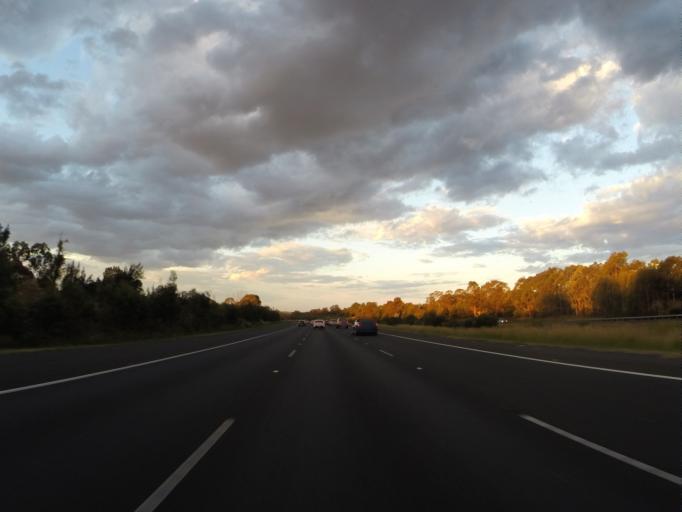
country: AU
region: New South Wales
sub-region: Campbelltown Municipality
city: Campbelltown
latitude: -34.0499
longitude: 150.8141
